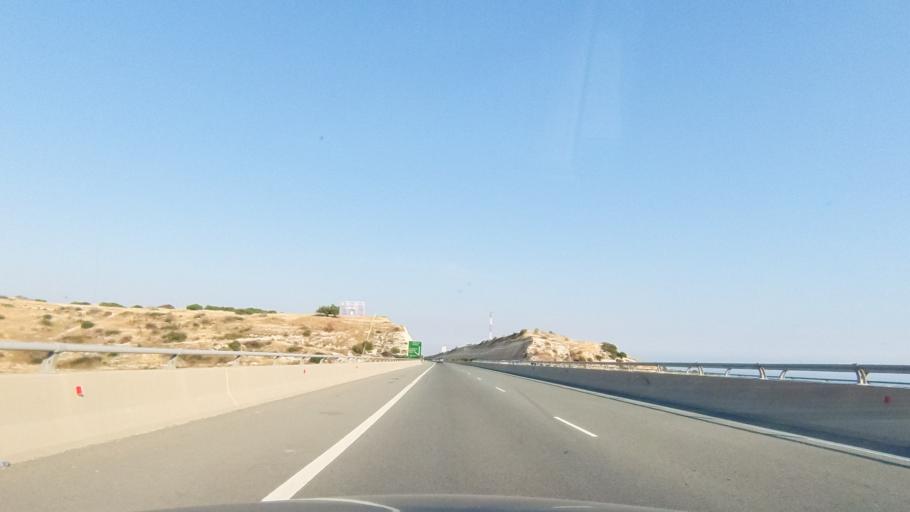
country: CY
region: Limassol
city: Sotira
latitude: 34.6880
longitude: 32.8739
